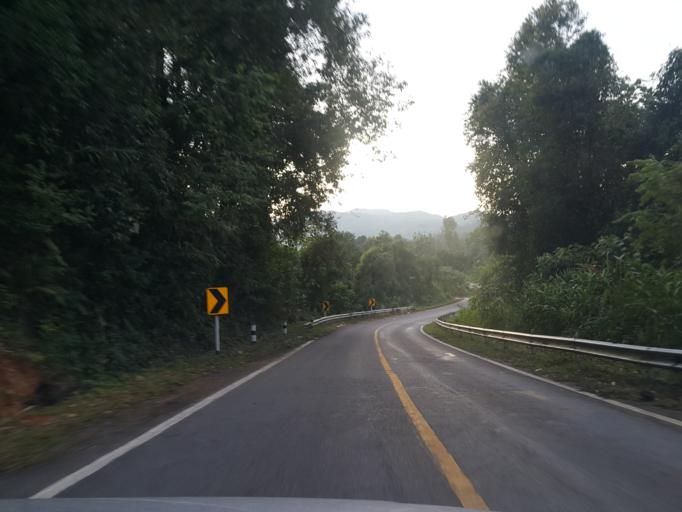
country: TH
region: Mae Hong Son
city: Khun Yuam
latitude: 18.8005
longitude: 98.0654
